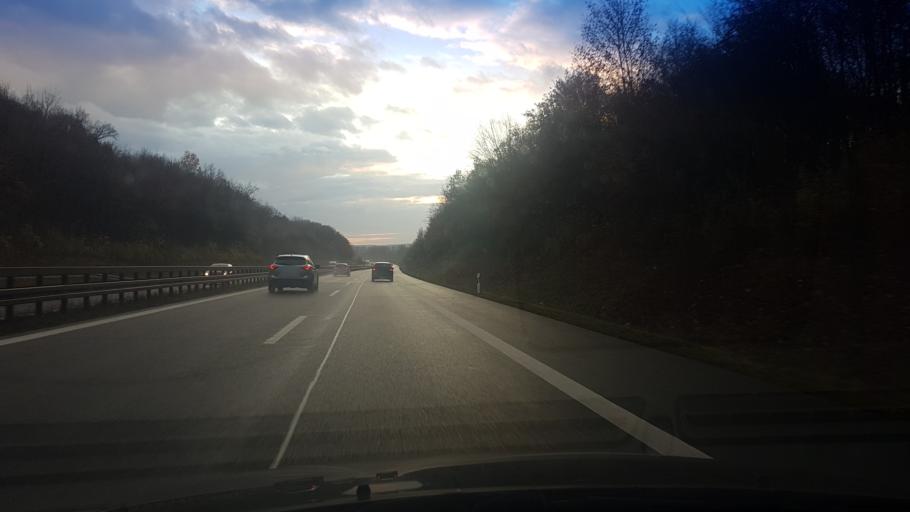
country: DE
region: Bavaria
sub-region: Upper Franconia
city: Zapfendorf
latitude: 50.0070
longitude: 10.9298
